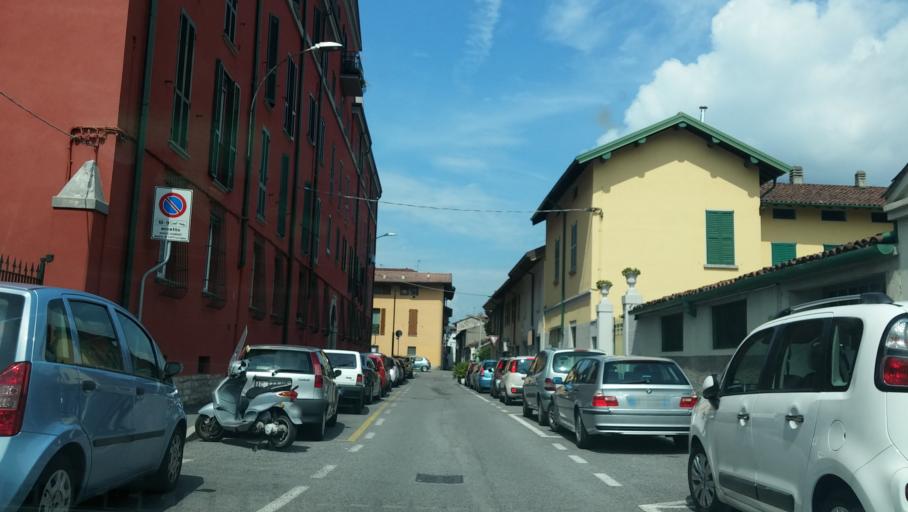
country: IT
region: Lombardy
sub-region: Provincia di Lecco
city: Pescate
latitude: 45.8434
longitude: 9.3997
